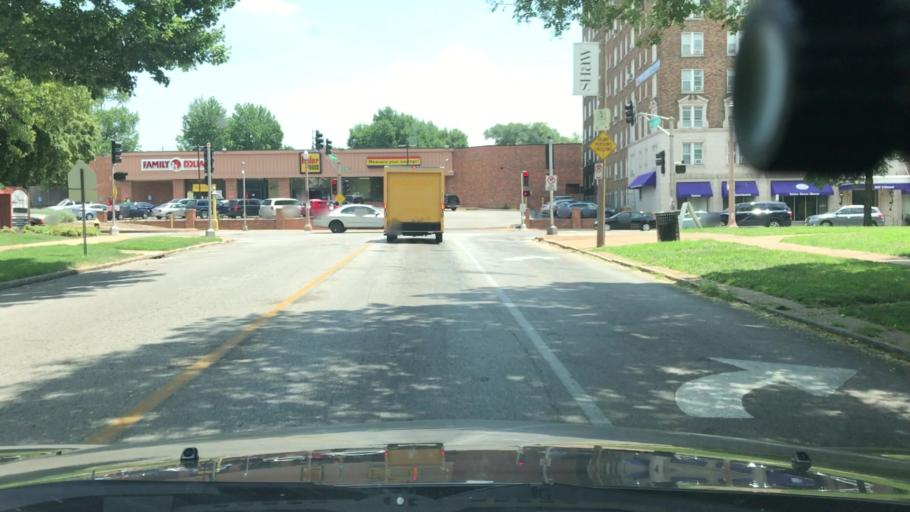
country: US
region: Missouri
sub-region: City of Saint Louis
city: St. Louis
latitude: 38.6073
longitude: -90.2420
